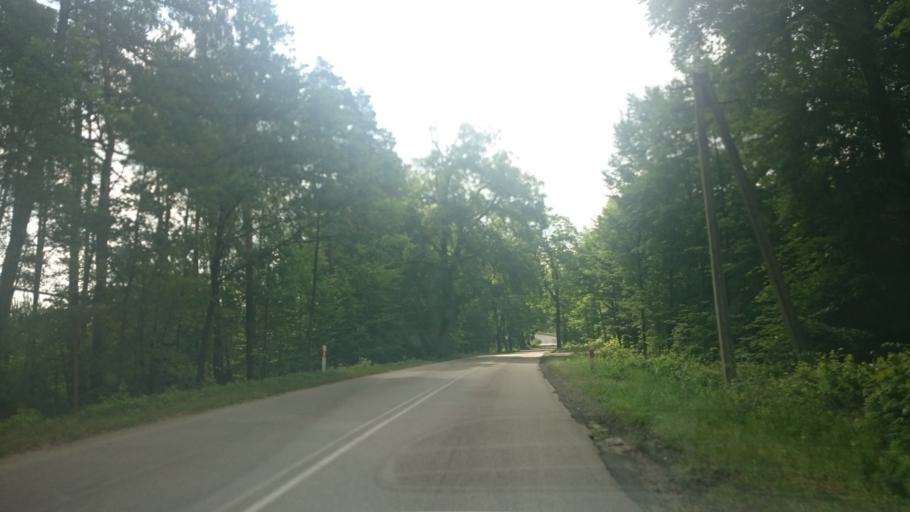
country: PL
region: Pomeranian Voivodeship
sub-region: Powiat starogardzki
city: Kaliska
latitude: 53.9711
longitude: 18.2434
